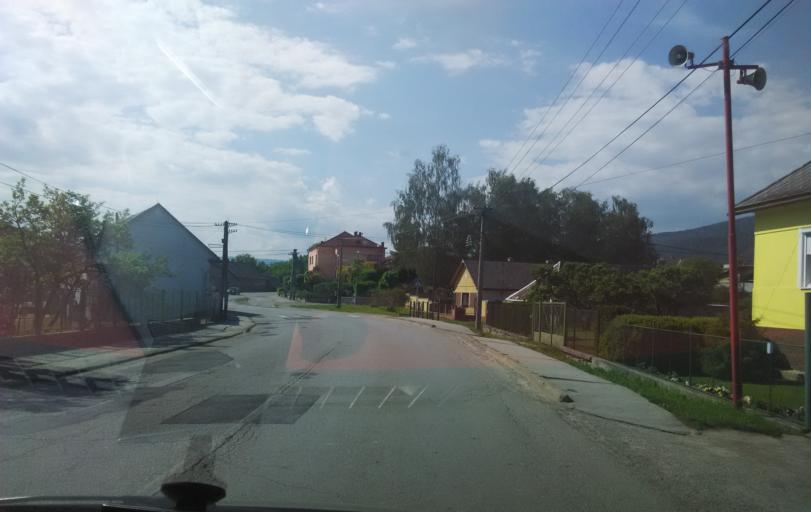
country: SK
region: Banskobystricky
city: Revuca
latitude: 48.6574
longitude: 20.1906
